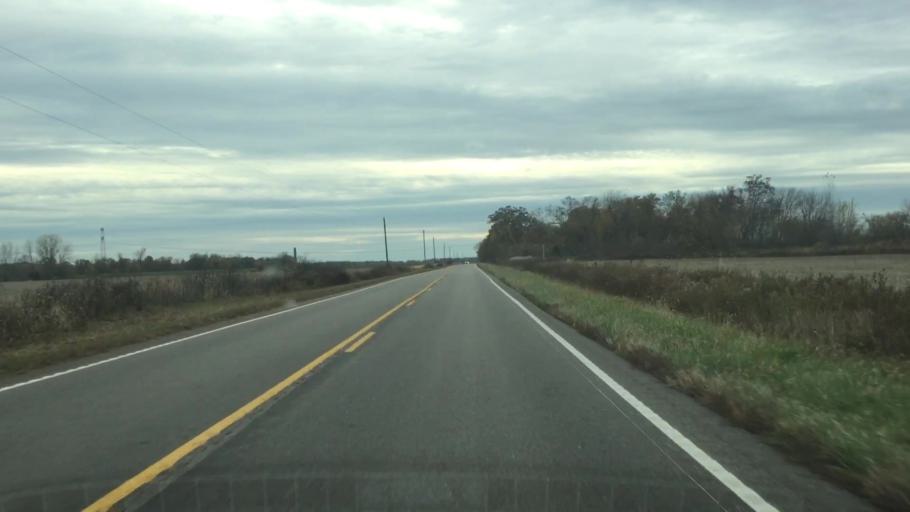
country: US
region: Missouri
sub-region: Callaway County
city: Fulton
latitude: 38.7080
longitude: -91.7570
